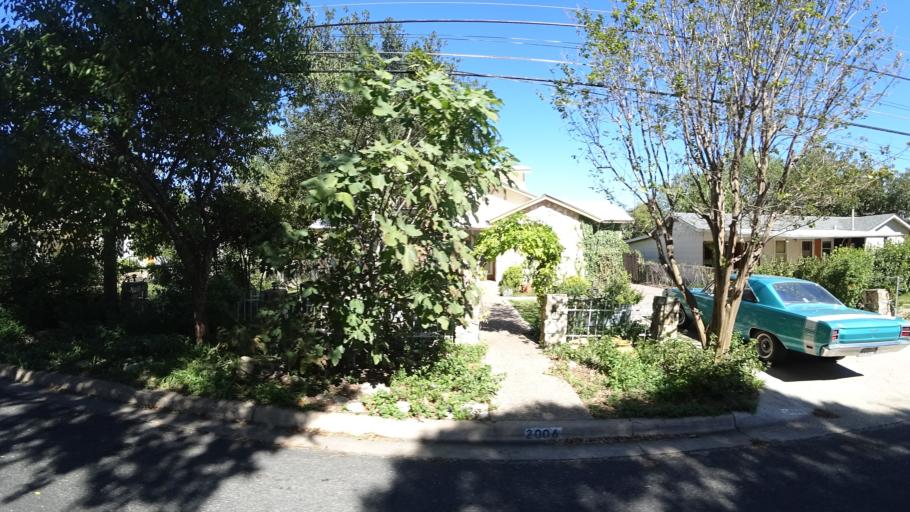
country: US
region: Texas
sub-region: Travis County
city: Austin
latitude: 30.3374
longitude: -97.7374
